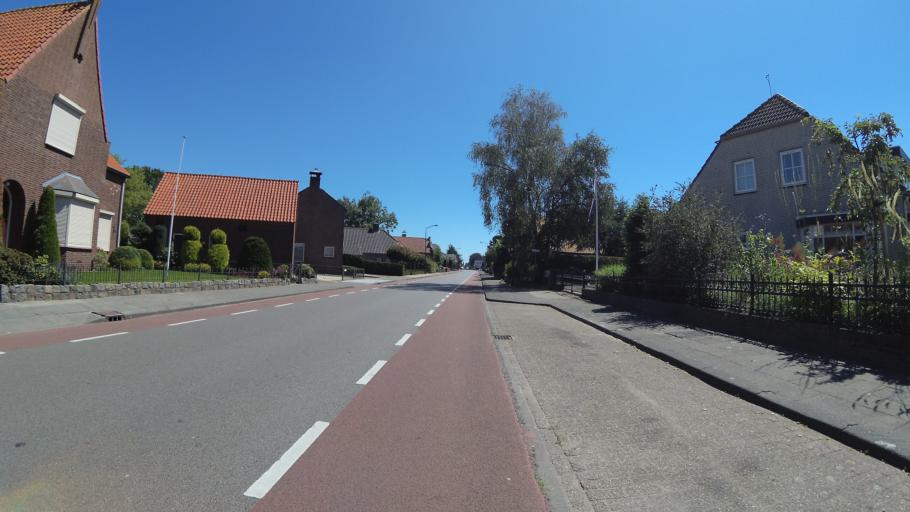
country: NL
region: North Brabant
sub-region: Gemeente Waalwijk
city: Waspik
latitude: 51.6776
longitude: 4.9951
